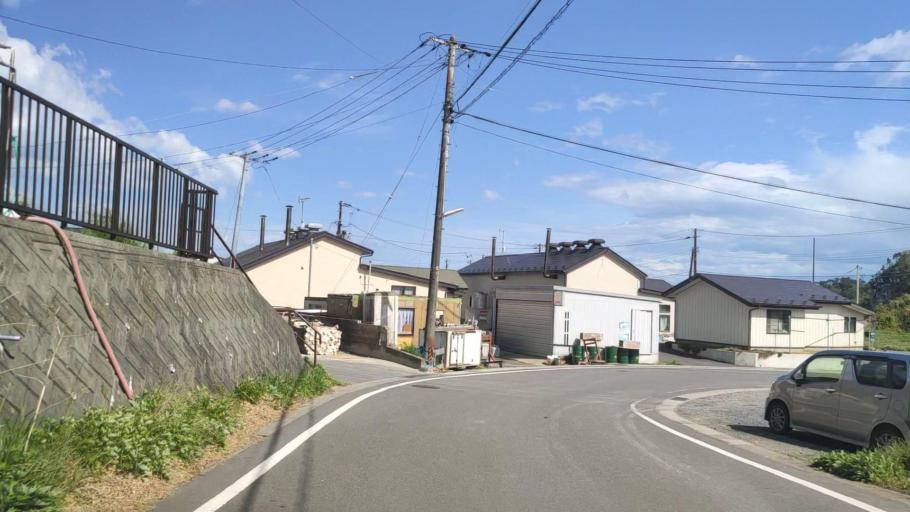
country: JP
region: Miyagi
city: Yamoto
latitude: 38.3356
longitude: 141.1648
